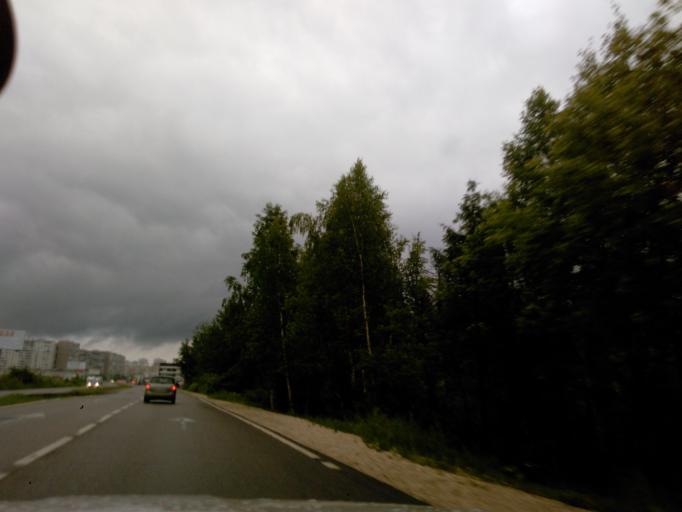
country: RU
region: Moskovskaya
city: Andreyevka
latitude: 55.9690
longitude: 37.1388
